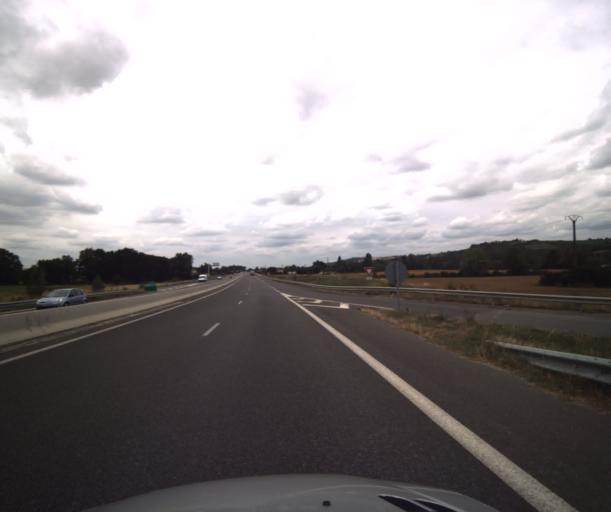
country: FR
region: Midi-Pyrenees
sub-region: Departement de la Haute-Garonne
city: Vernet
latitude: 43.4489
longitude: 1.4198
